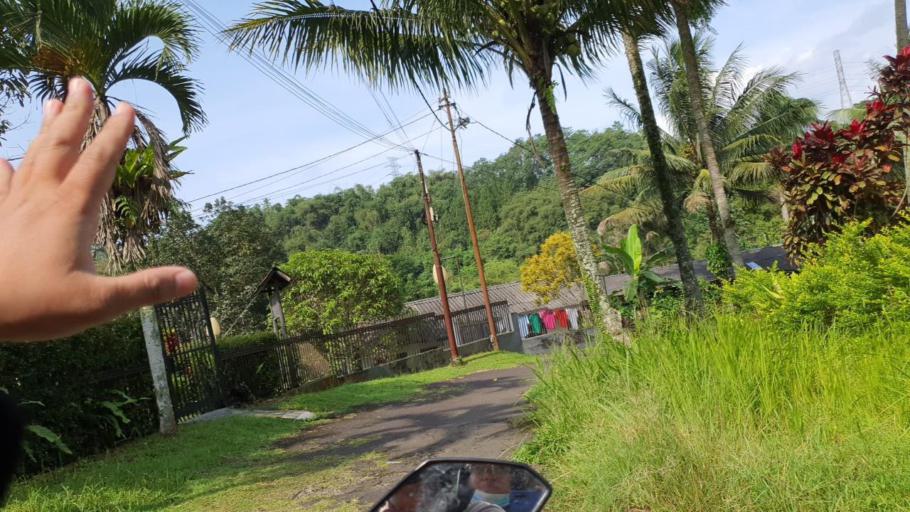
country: ID
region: West Java
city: Caringin
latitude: -6.6560
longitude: 106.8725
